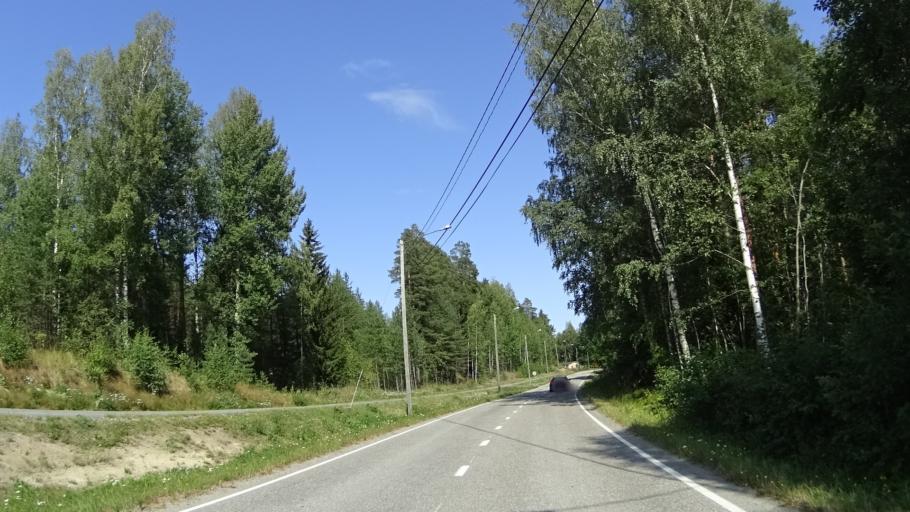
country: FI
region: Pirkanmaa
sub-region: Ylae-Pirkanmaa
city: Maenttae
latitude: 61.8578
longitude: 24.8227
